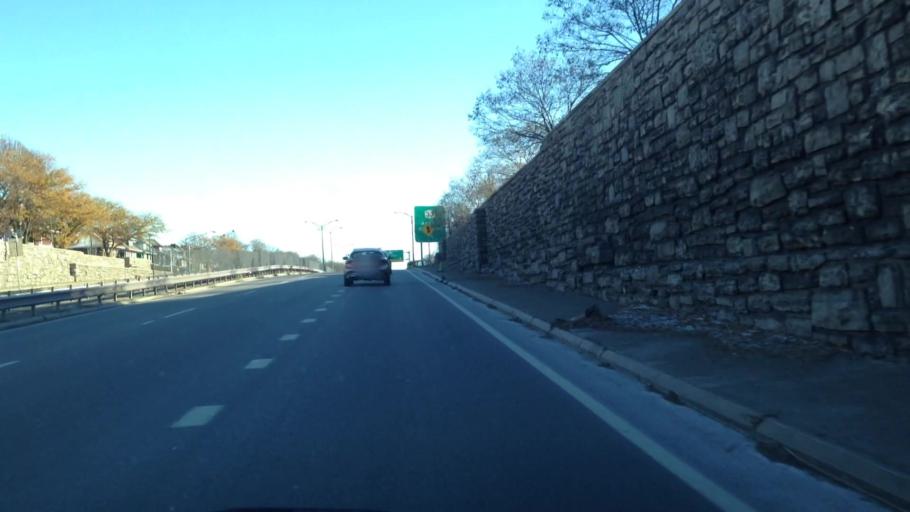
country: US
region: New York
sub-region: Erie County
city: Kenmore
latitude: 42.9273
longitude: -78.8501
